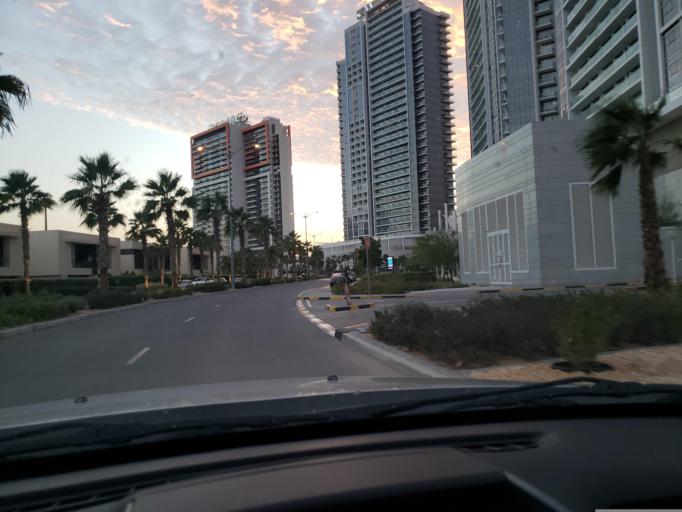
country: AE
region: Dubai
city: Dubai
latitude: 25.0254
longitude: 55.2452
